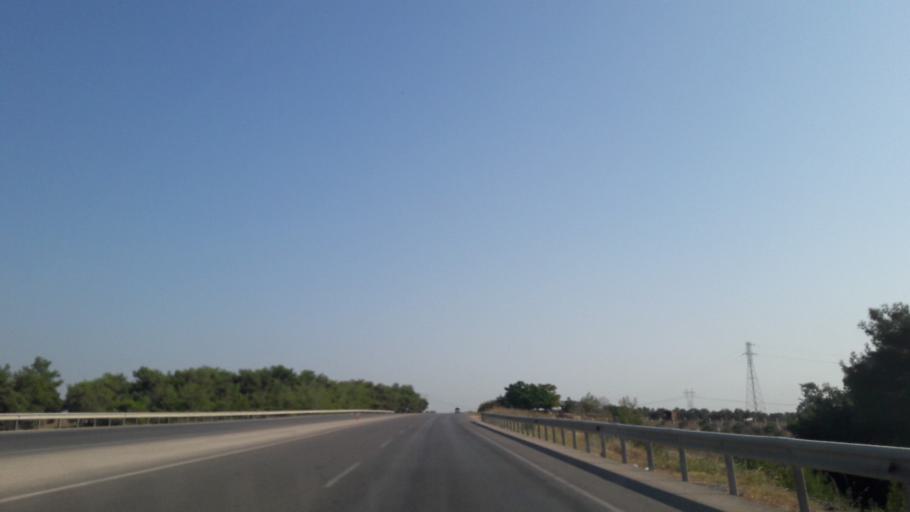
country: TR
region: Adana
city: Sagkaya
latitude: 37.1266
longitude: 35.5187
